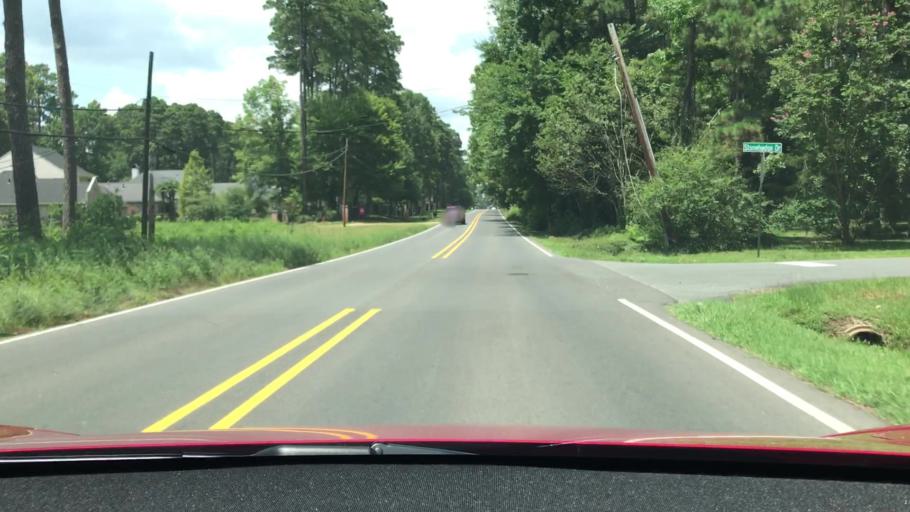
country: US
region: Louisiana
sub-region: Bossier Parish
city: Bossier City
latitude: 32.3775
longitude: -93.7138
